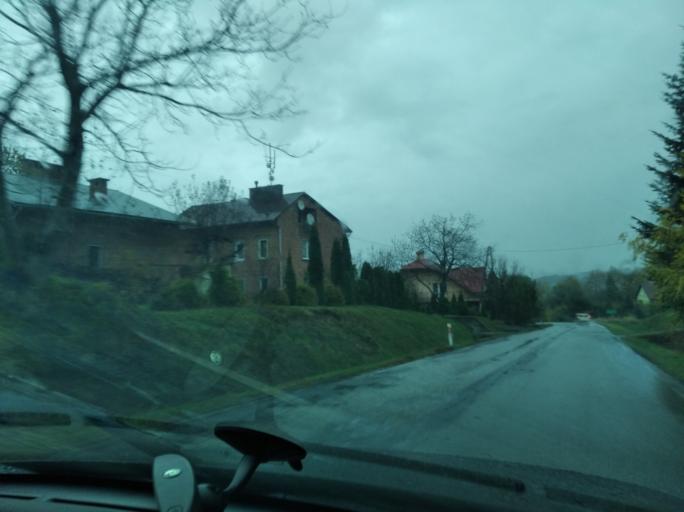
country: PL
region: Subcarpathian Voivodeship
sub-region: Powiat lancucki
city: Handzlowka
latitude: 50.0034
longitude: 22.2062
